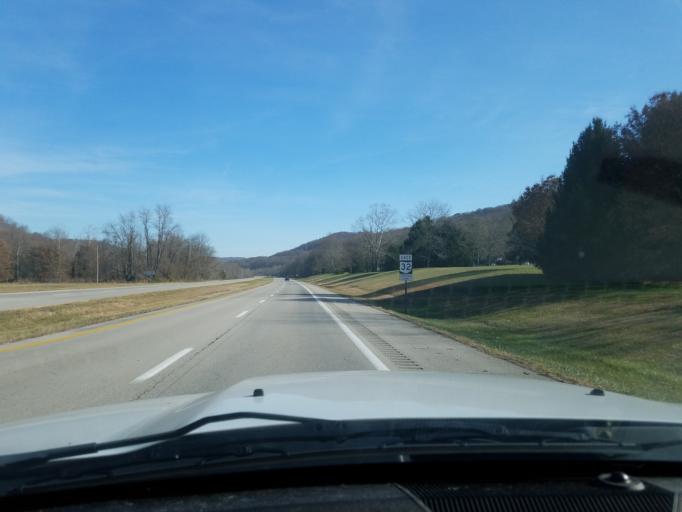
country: US
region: Ohio
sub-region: Adams County
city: Peebles
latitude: 39.0419
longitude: -83.2316
